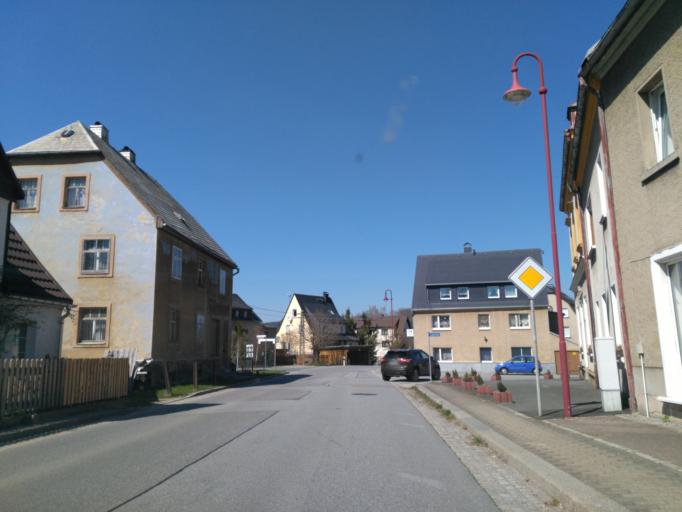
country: DE
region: Saxony
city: Crottendorf
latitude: 50.5079
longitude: 12.9359
